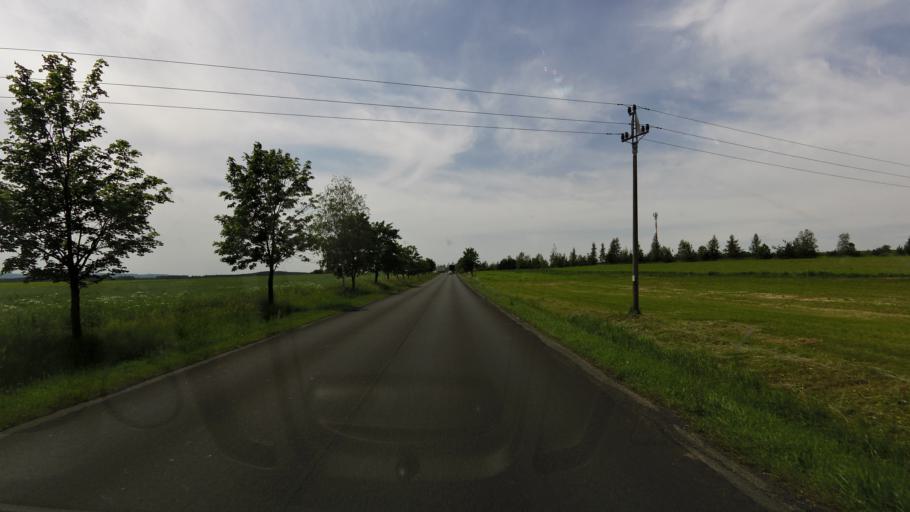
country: CZ
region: Plzensky
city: Zbiroh
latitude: 49.8213
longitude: 13.7733
